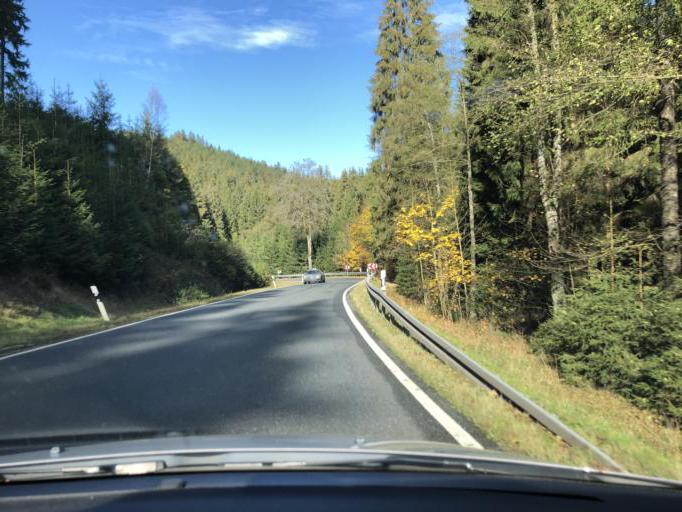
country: DE
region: Thuringia
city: Katzhutte
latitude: 50.5344
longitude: 11.0895
